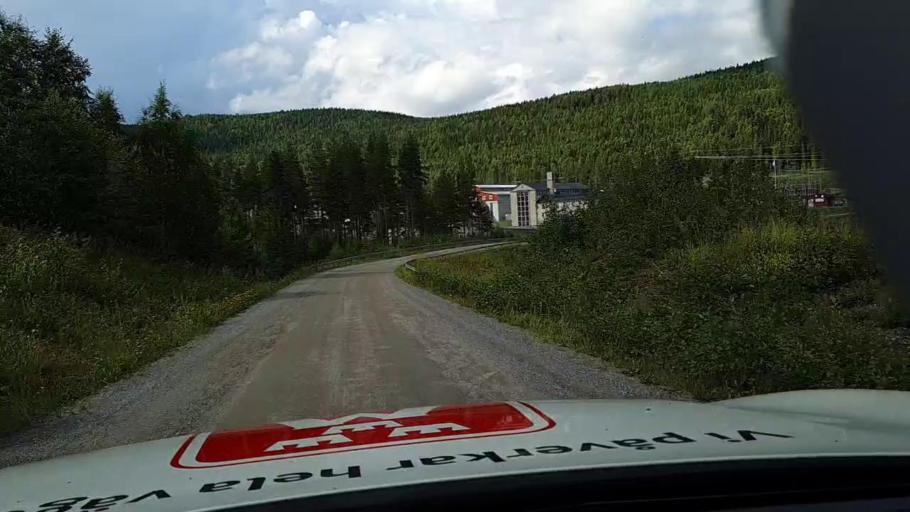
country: SE
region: Jaemtland
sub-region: Ragunda Kommun
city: Hammarstrand
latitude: 63.1444
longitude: 16.0753
